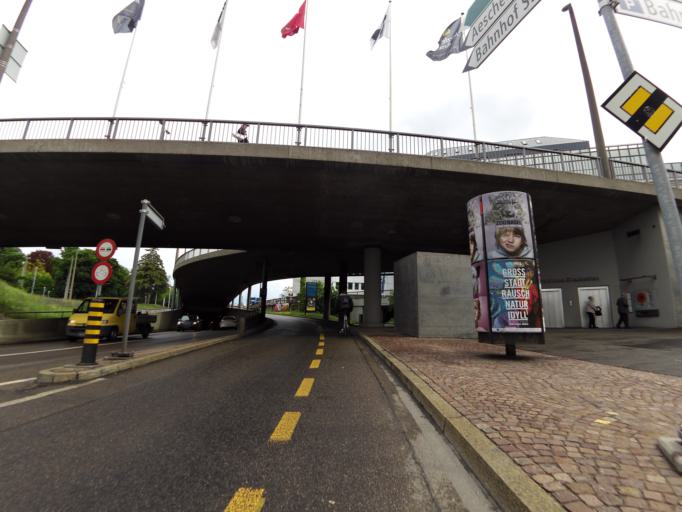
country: CH
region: Basel-City
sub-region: Basel-Stadt
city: Basel
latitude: 47.5495
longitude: 7.5882
